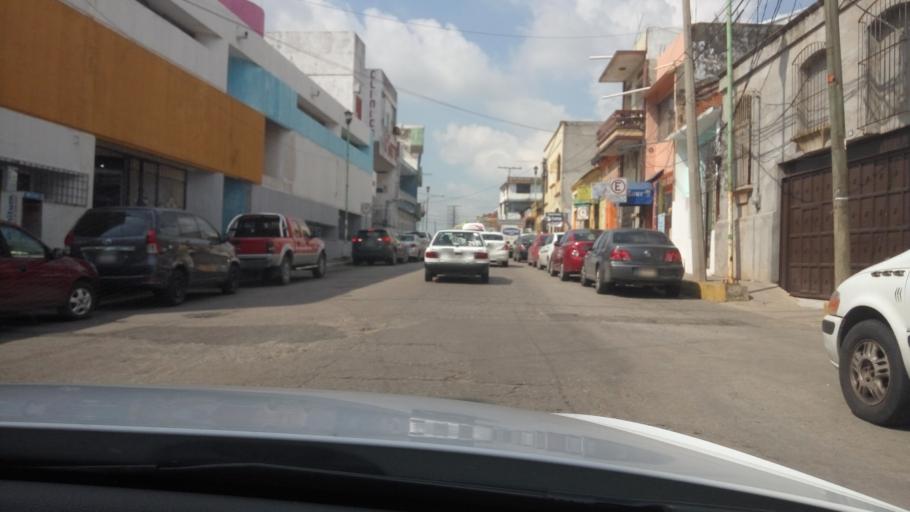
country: MX
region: Tabasco
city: Villahermosa
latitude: 17.9906
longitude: -92.9217
